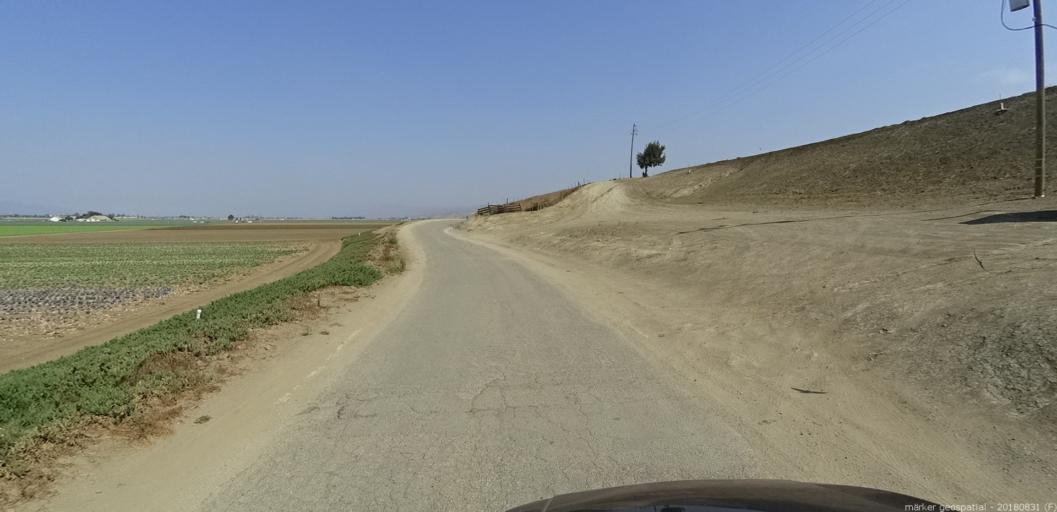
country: US
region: California
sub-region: Monterey County
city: Greenfield
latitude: 36.3043
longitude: -121.2053
